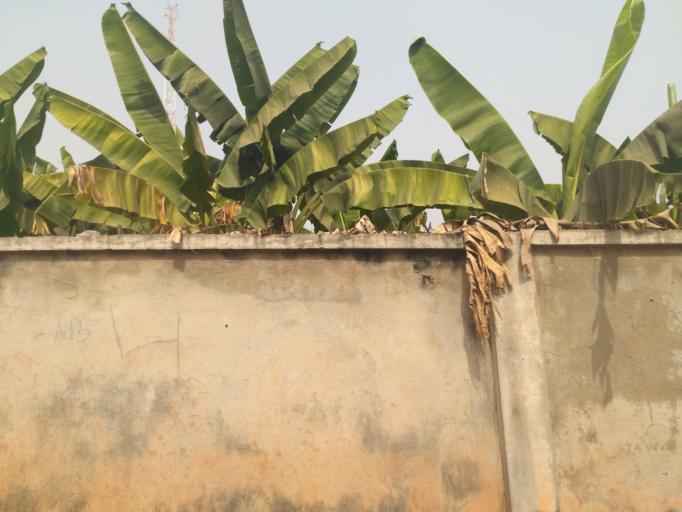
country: GH
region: Ashanti
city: Kumasi
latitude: 6.6744
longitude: -1.6002
